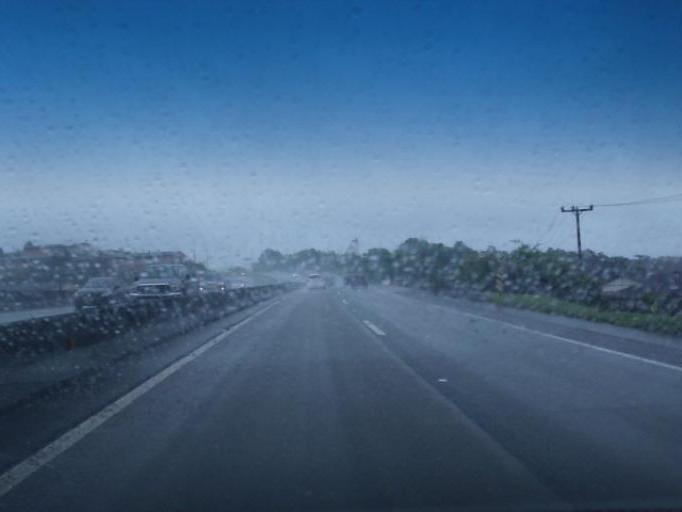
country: BR
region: Santa Catarina
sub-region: Joinville
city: Joinville
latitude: -26.3387
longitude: -48.8592
